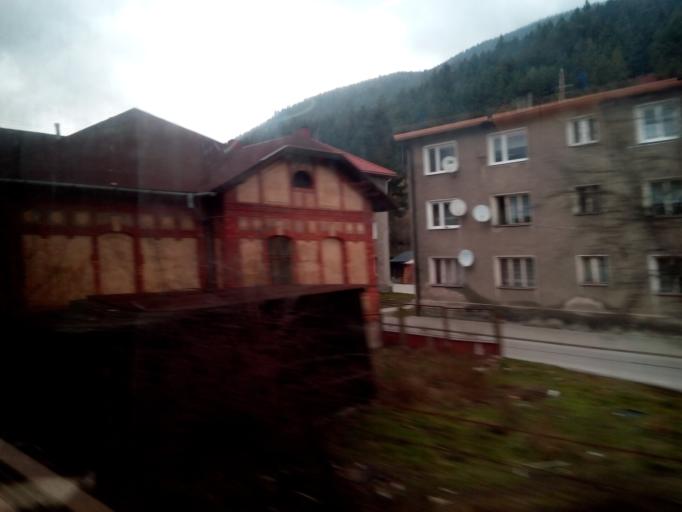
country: SK
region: Zilinsky
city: Ruzomberok
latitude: 49.0869
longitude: 19.2785
